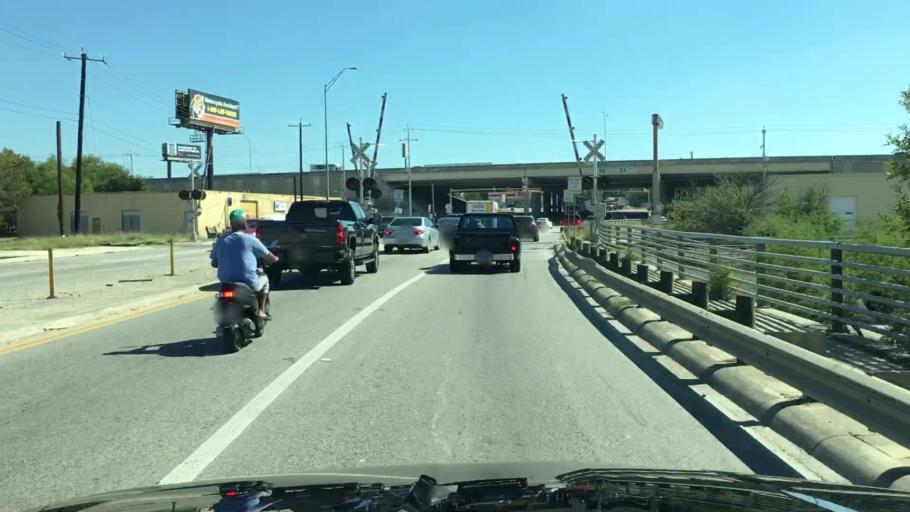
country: US
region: Texas
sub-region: Bexar County
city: Windcrest
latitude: 29.5341
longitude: -98.3911
